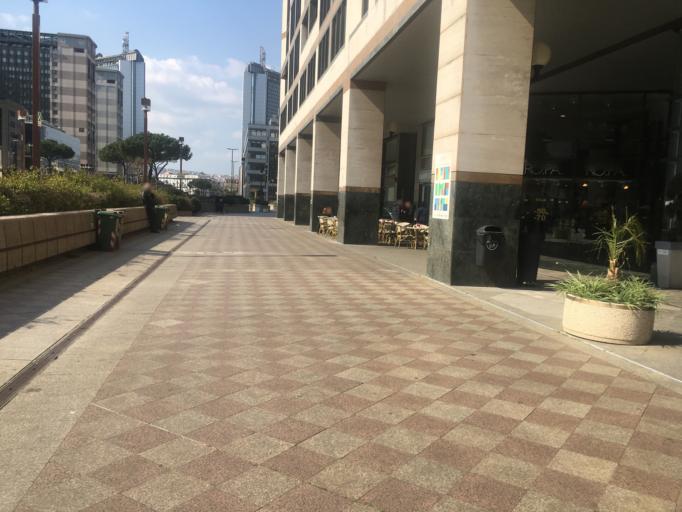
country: IT
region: Campania
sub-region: Provincia di Napoli
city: Napoli
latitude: 40.8574
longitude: 14.2832
